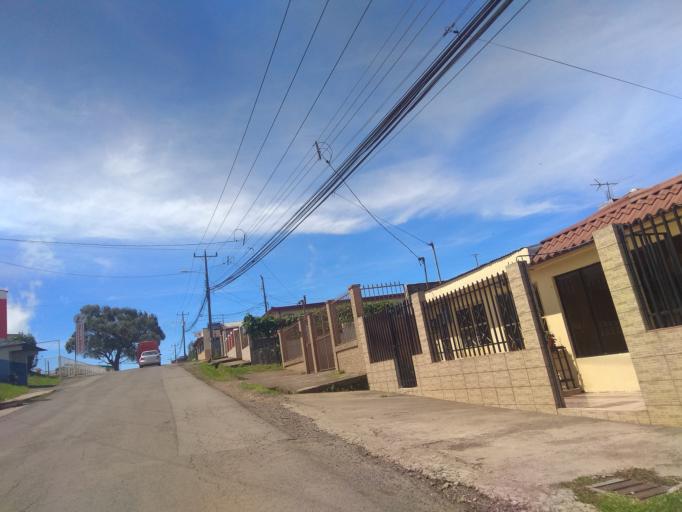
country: CR
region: Cartago
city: Cot
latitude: 9.9132
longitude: -83.8882
